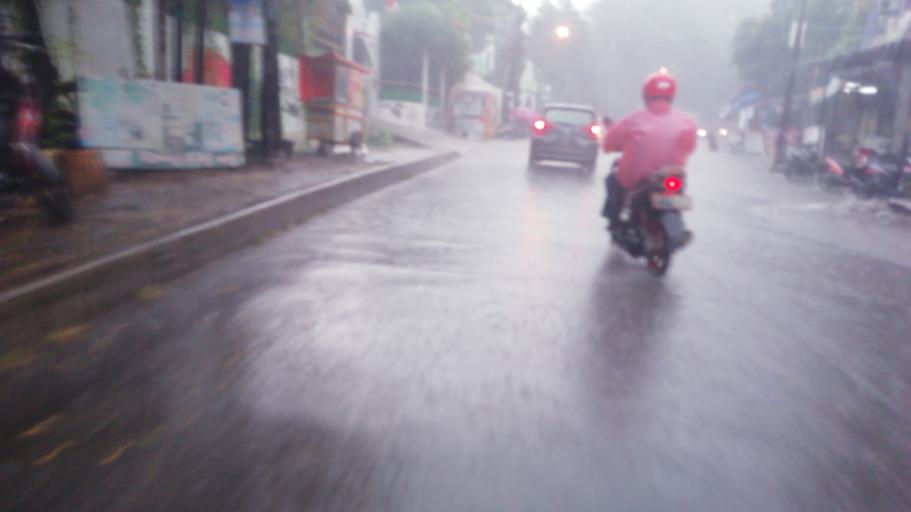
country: ID
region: West Java
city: Depok
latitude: -6.3540
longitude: 106.8370
